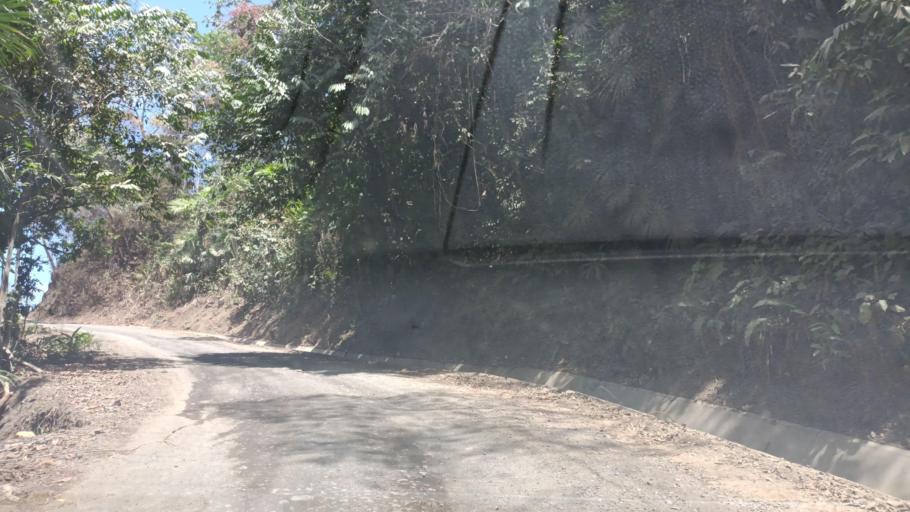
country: PA
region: Panama
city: Alcalde Diaz
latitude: 9.0758
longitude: -79.5744
